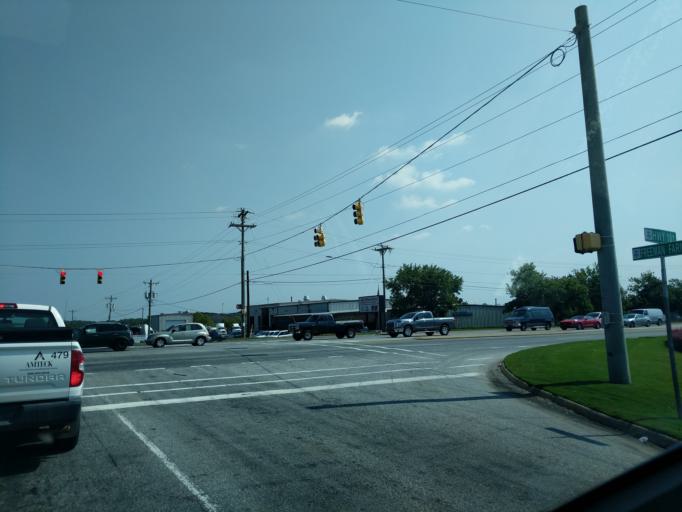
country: US
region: South Carolina
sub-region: Spartanburg County
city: Duncan
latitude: 34.8902
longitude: -82.1579
